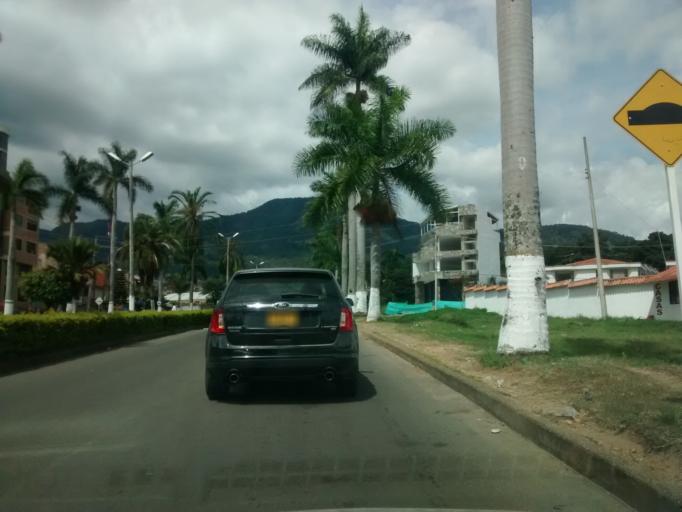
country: CO
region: Cundinamarca
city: Fusagasuga
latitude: 4.3434
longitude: -74.3741
